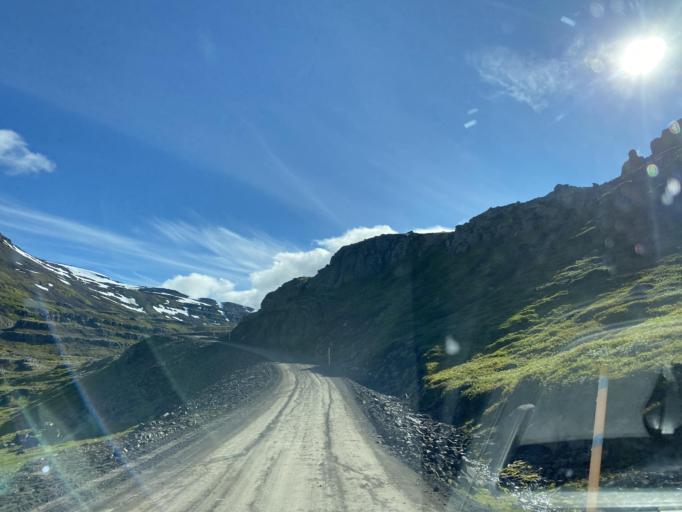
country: IS
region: East
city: Eskifjoerdur
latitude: 65.1794
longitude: -14.0958
